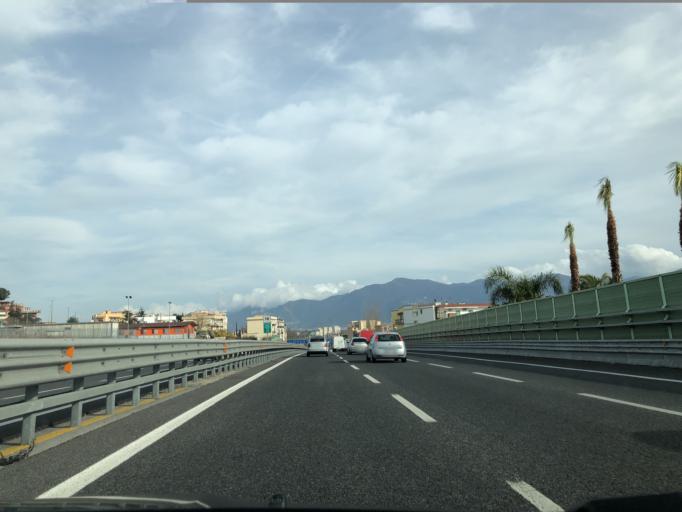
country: IT
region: Campania
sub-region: Provincia di Napoli
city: Trecase
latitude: 40.7644
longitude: 14.4360
